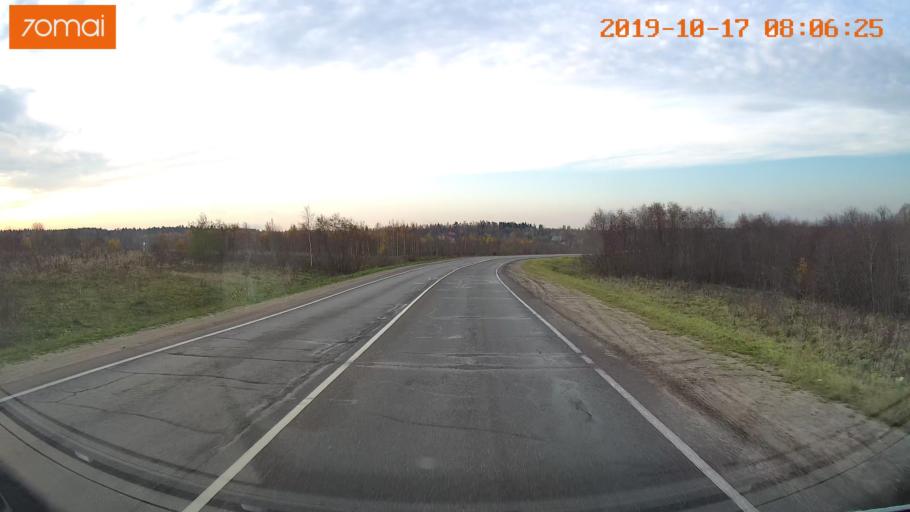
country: RU
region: Vladimir
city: Kol'chugino
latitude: 56.3231
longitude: 39.4136
